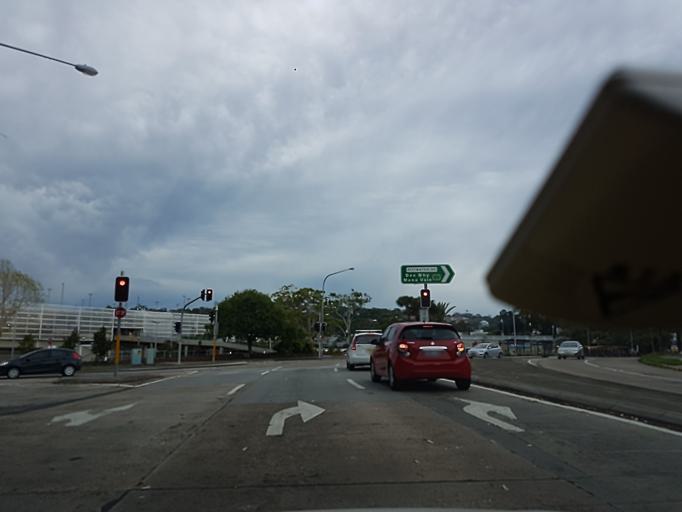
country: AU
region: New South Wales
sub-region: Warringah
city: North Manly
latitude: -33.7686
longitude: 151.2680
